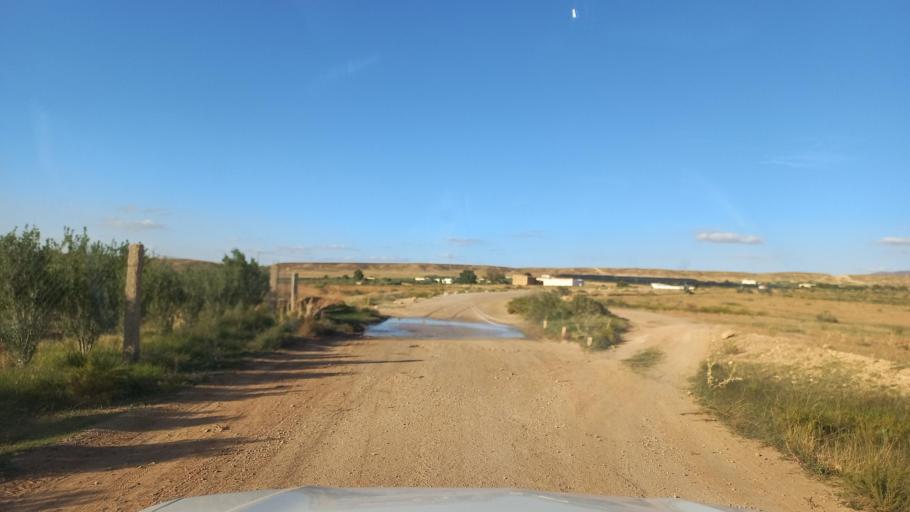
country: TN
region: Al Qasrayn
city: Sbiba
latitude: 35.3397
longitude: 9.1195
